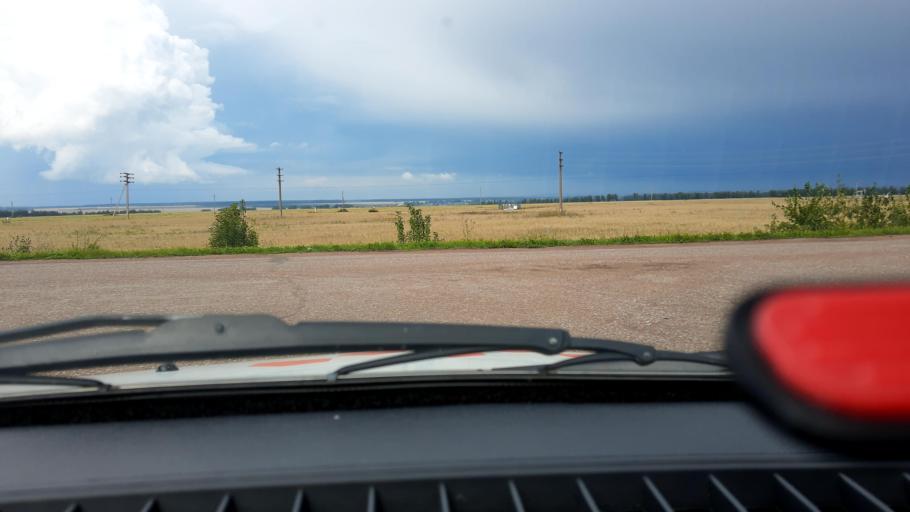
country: RU
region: Bashkortostan
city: Semiletka
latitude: 55.3646
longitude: 54.6148
